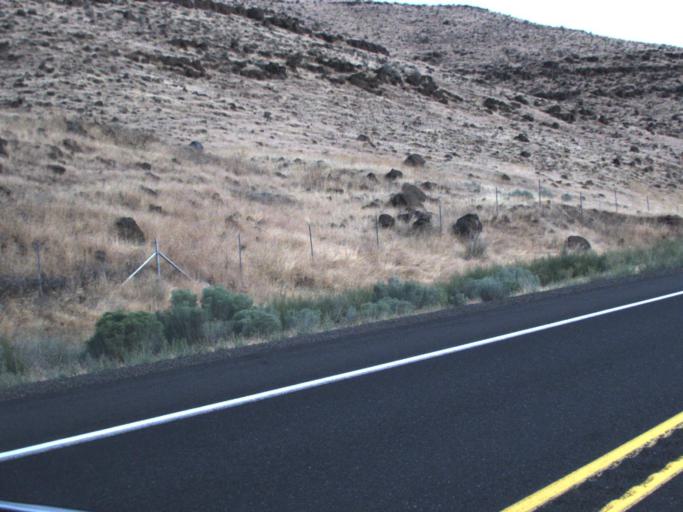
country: US
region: Washington
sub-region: Yakima County
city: Toppenish
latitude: 46.1993
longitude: -120.4856
